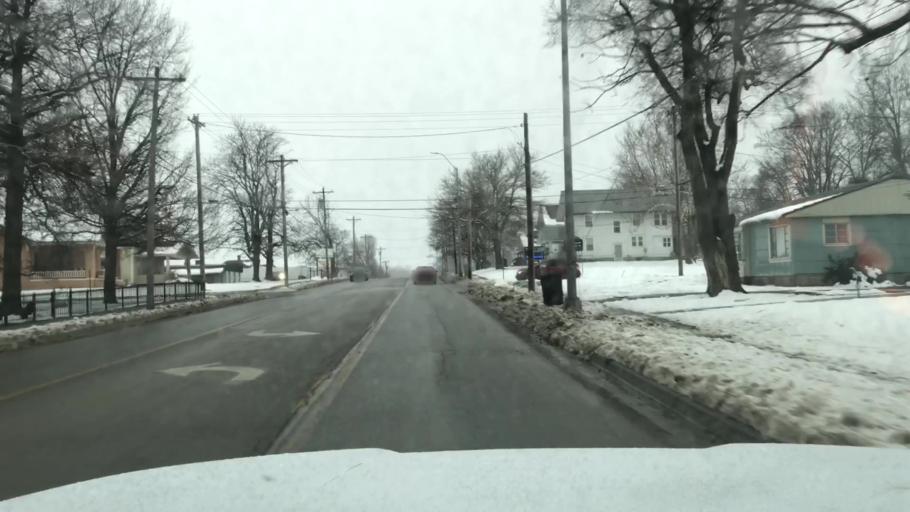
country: US
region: Missouri
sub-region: Clinton County
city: Cameron
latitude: 39.7347
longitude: -94.2361
